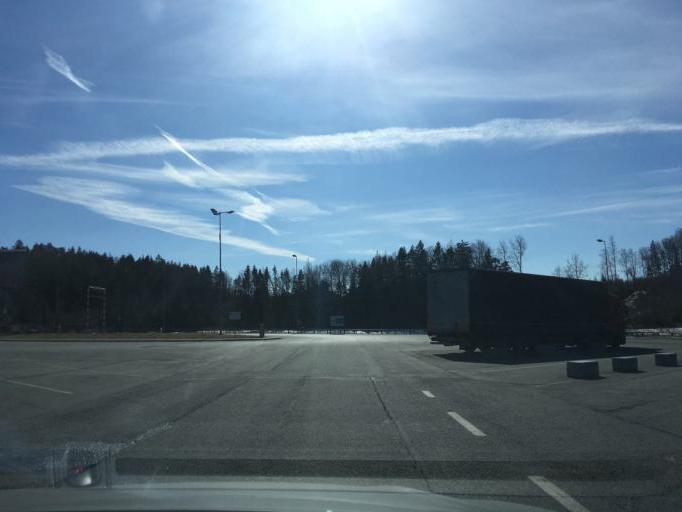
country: NO
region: Ostfold
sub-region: Sarpsborg
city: Skjeberg
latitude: 59.1085
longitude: 11.2618
